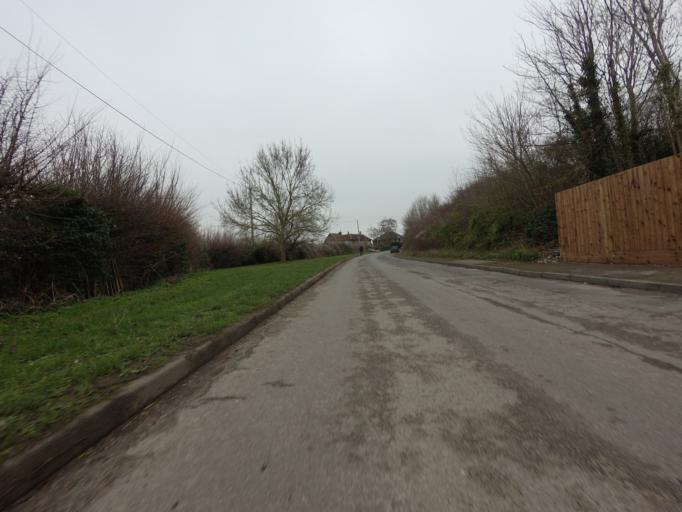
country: GB
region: England
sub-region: Kent
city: Eynsford
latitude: 51.3904
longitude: 0.2441
